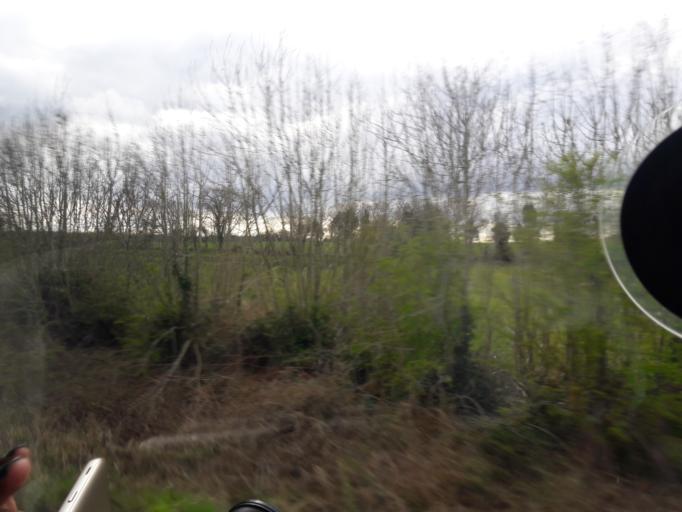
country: IE
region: Leinster
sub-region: An Longfort
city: Longford
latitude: 53.7286
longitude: -7.8181
